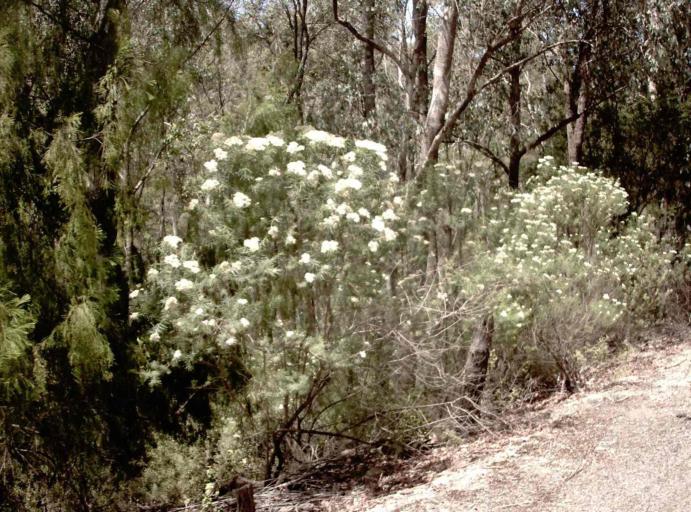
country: AU
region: Victoria
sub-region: East Gippsland
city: Lakes Entrance
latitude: -37.5760
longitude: 147.8960
